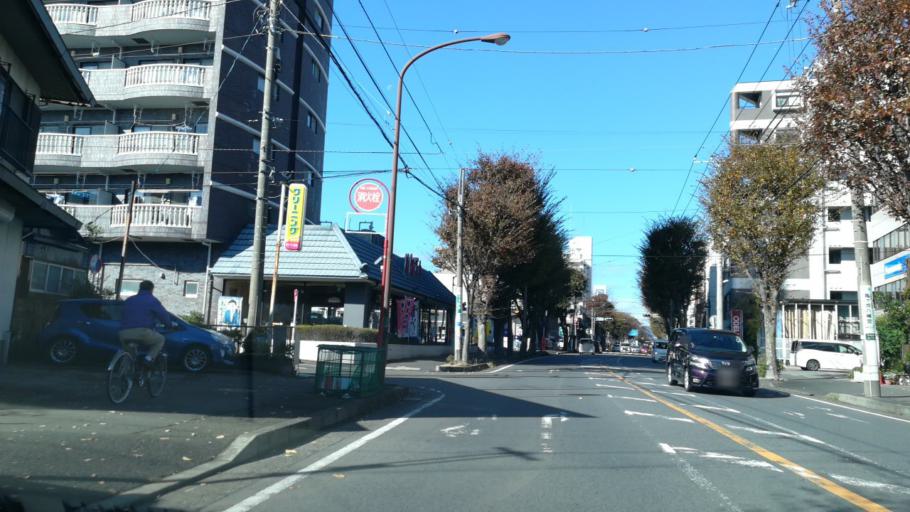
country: JP
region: Kanagawa
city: Zama
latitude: 35.5636
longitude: 139.3728
